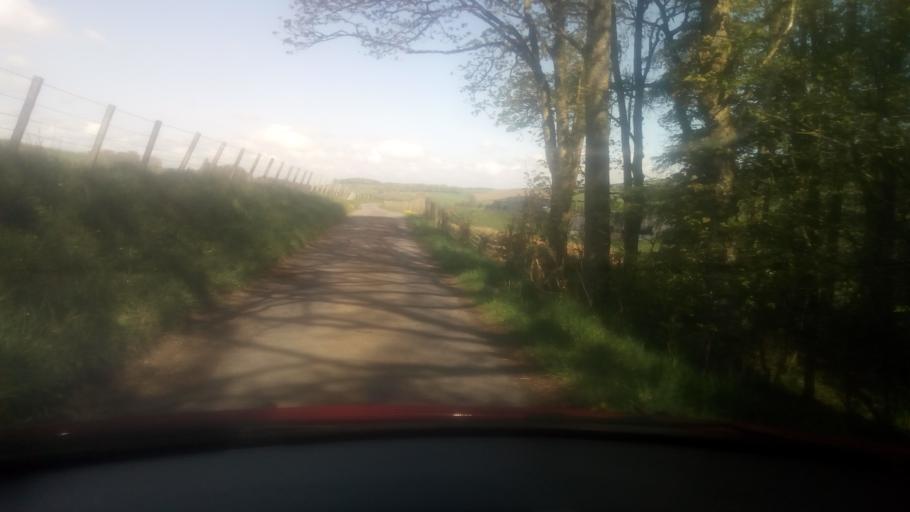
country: GB
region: Scotland
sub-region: The Scottish Borders
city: Hawick
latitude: 55.4268
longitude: -2.7069
